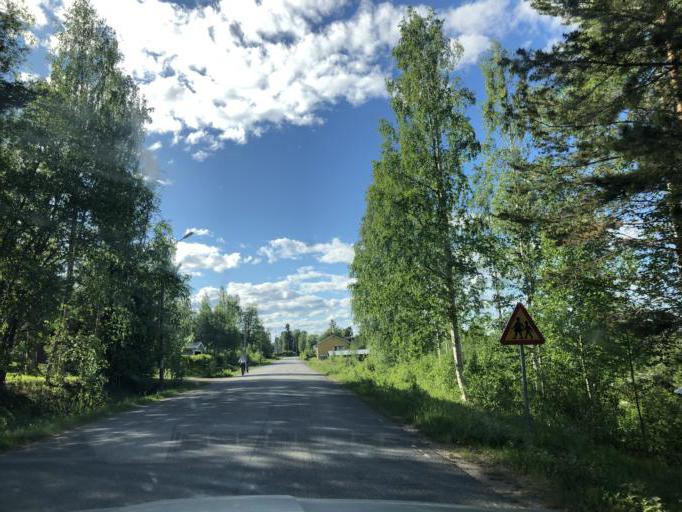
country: SE
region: Norrbotten
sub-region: Overkalix Kommun
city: OEverkalix
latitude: 66.3195
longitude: 22.8656
